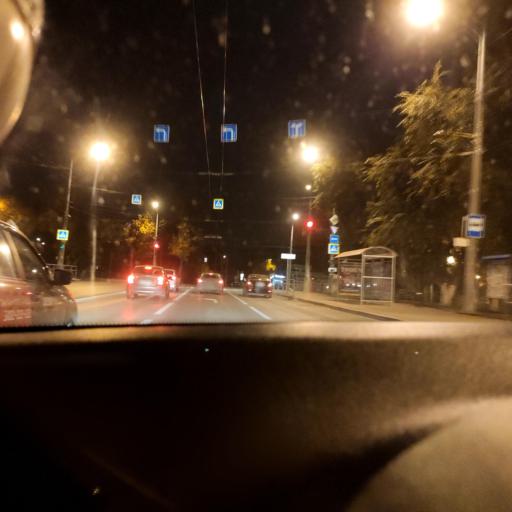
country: RU
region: Samara
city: Samara
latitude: 53.2050
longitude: 50.1635
